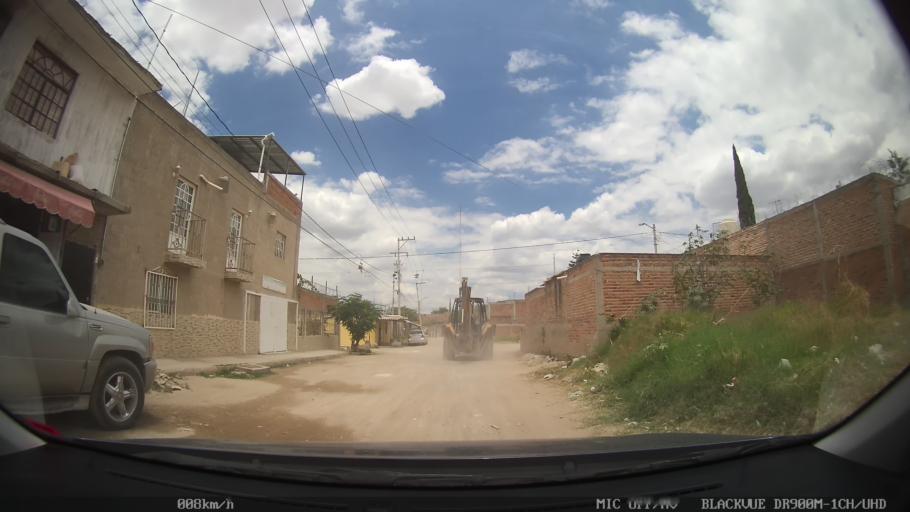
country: MX
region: Jalisco
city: Tlaquepaque
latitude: 20.6433
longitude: -103.2685
